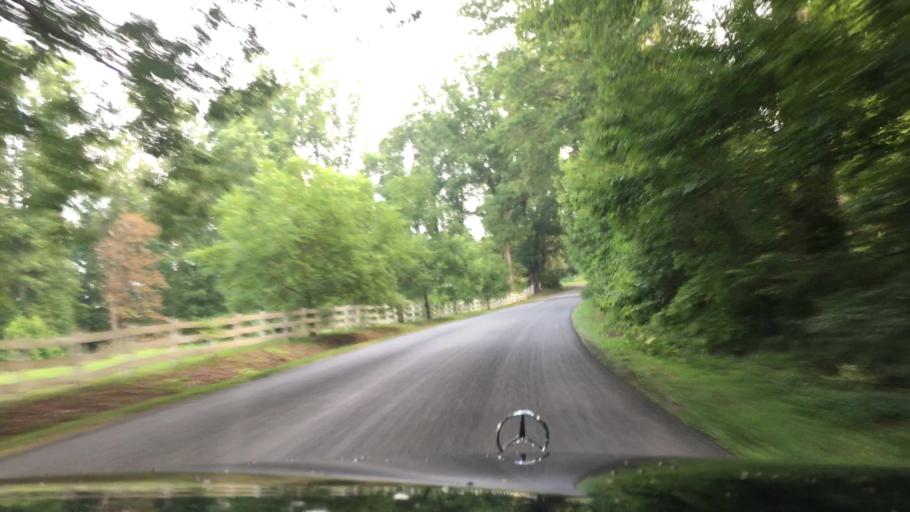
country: US
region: Virginia
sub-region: Campbell County
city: Timberlake
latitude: 37.2519
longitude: -79.3124
